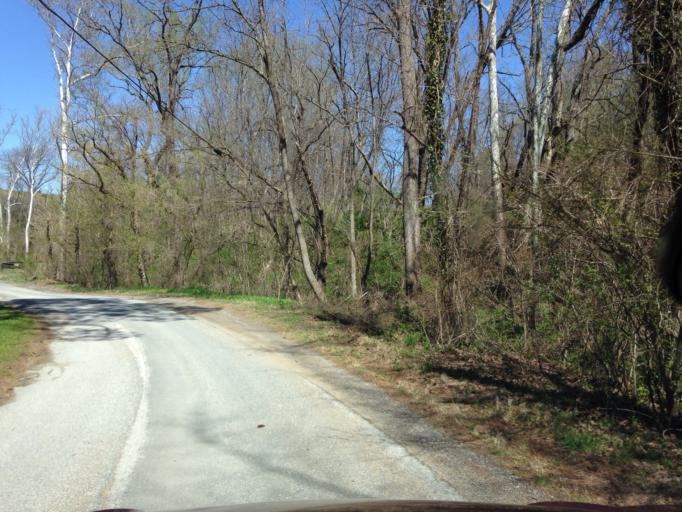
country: US
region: Maryland
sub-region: Frederick County
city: Brunswick
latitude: 39.2986
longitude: -77.6338
